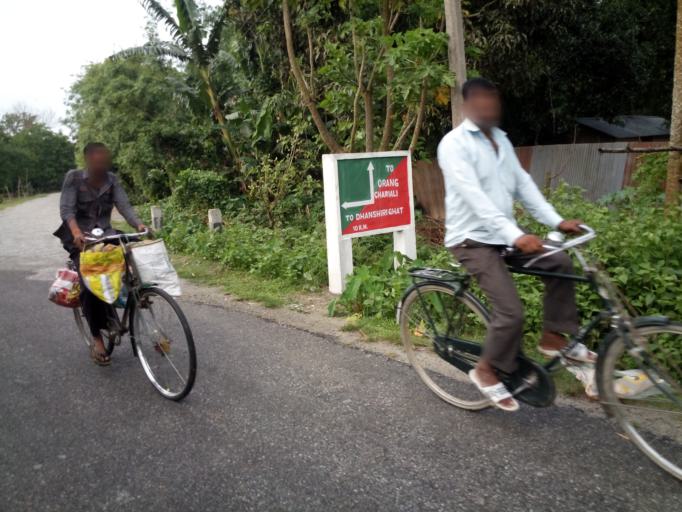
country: IN
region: Assam
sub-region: Darrang
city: Kharupatia
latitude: 26.6197
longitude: 92.2908
